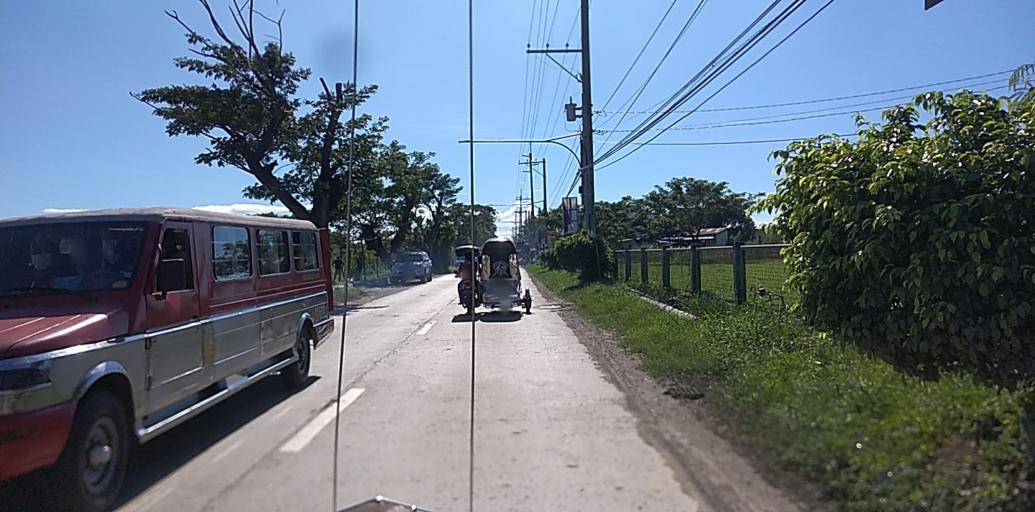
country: PH
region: Central Luzon
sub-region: Province of Pampanga
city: San Luis
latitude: 15.0472
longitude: 120.7855
